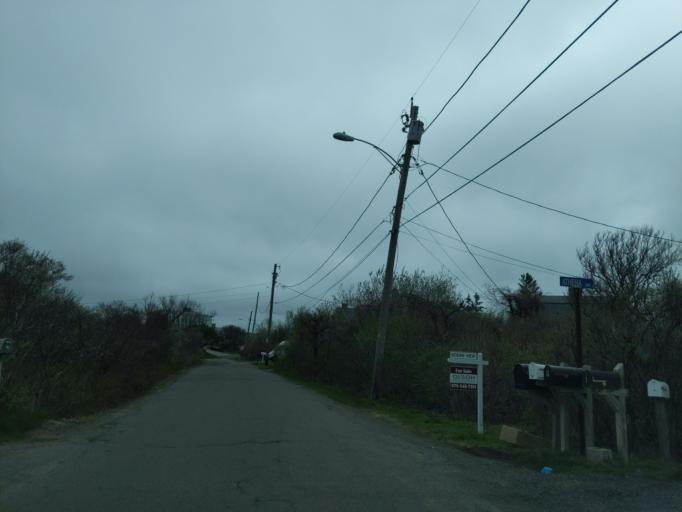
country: US
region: Massachusetts
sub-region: Essex County
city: Rockport
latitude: 42.6483
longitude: -70.5944
